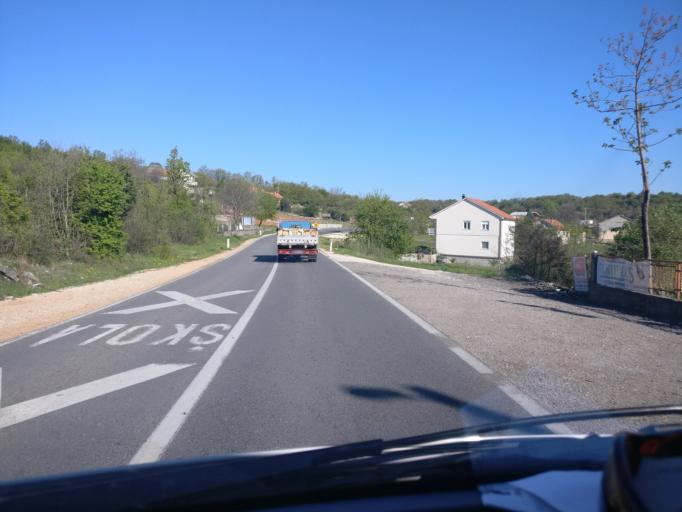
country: BA
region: Federation of Bosnia and Herzegovina
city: Crnici
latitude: 43.1062
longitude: 17.9060
